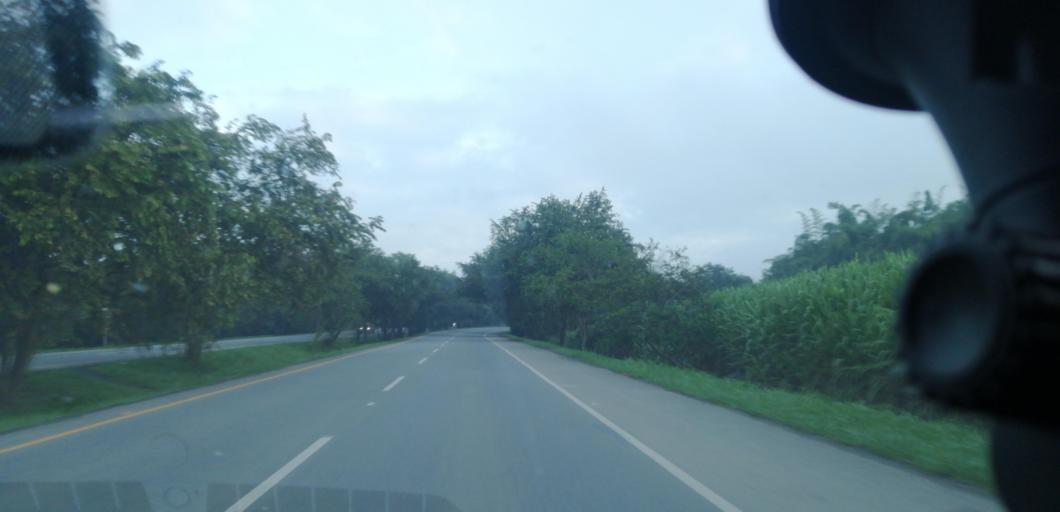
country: CO
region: Valle del Cauca
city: Palmira
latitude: 3.5647
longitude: -76.3335
